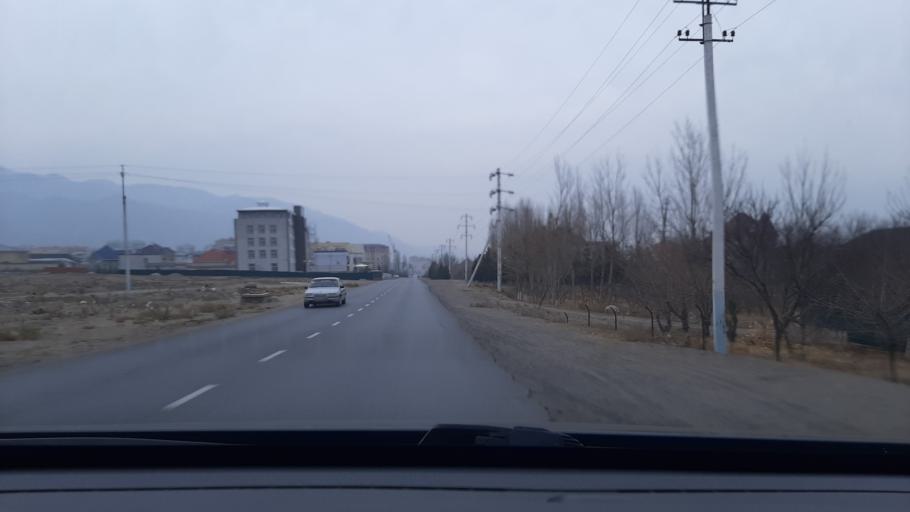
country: TJ
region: Viloyati Sughd
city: Khujand
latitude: 40.2775
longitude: 69.5815
